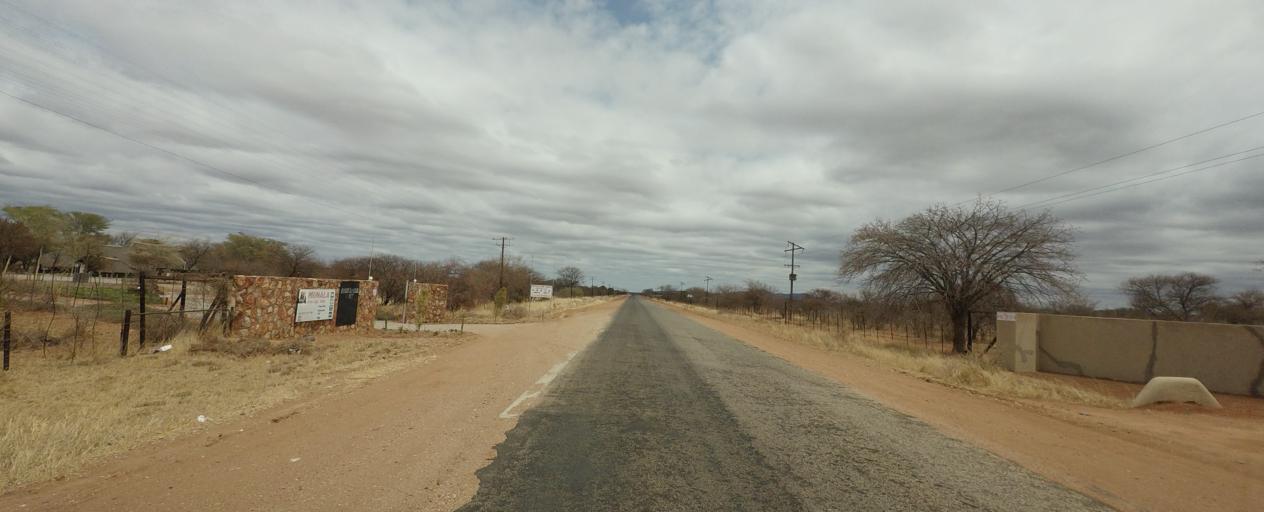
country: BW
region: Central
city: Mathathane
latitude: -22.6769
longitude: 29.0969
